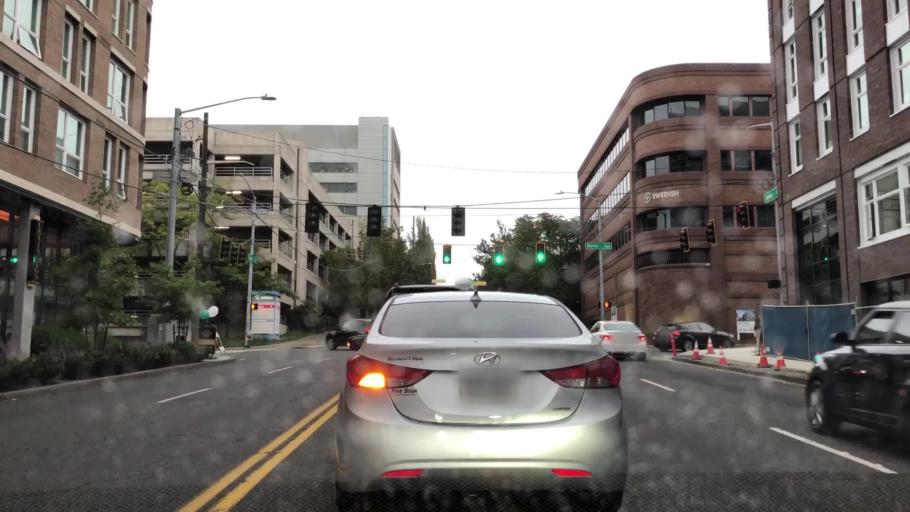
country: US
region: Washington
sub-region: Kitsap County
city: Manchester
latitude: 47.5763
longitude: -122.4931
